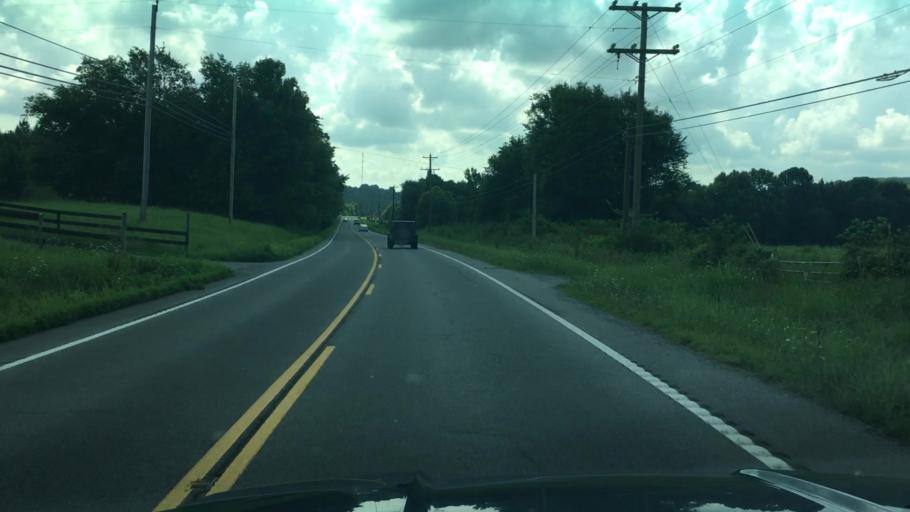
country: US
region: Tennessee
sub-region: Williamson County
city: Nolensville
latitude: 35.8587
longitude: -86.6782
